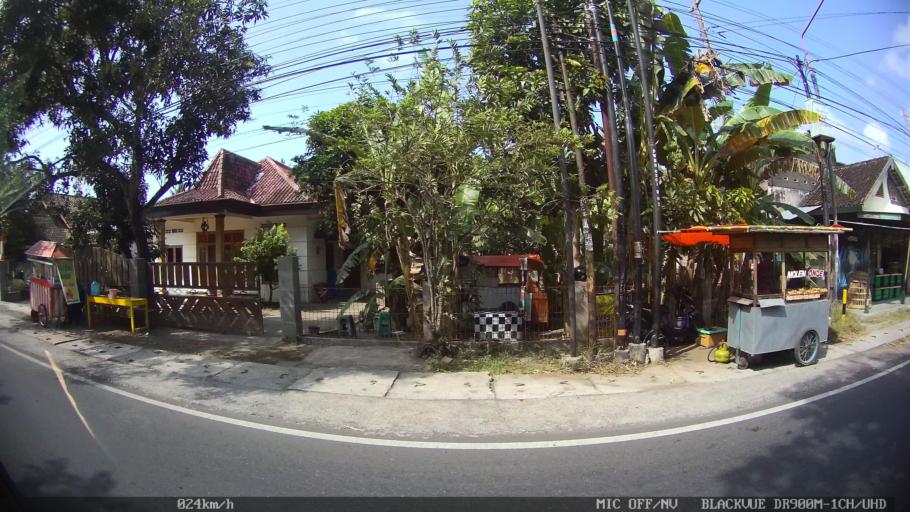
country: ID
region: Daerah Istimewa Yogyakarta
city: Srandakan
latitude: -7.8939
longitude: 110.1443
